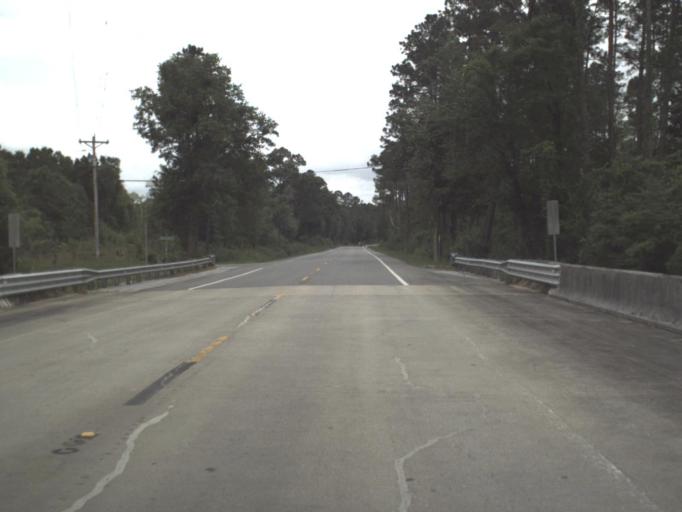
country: US
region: Florida
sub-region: Santa Rosa County
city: Point Baker
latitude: 30.8023
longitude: -87.0423
